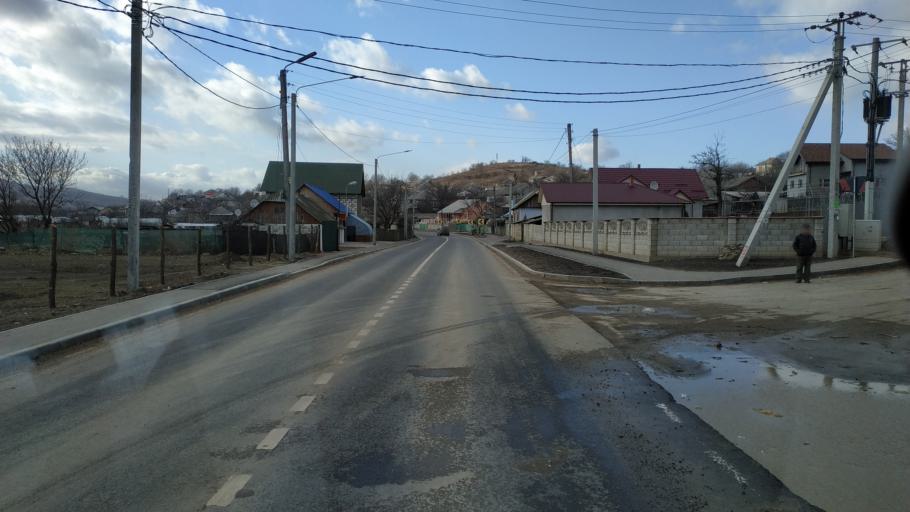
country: MD
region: Calarasi
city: Calarasi
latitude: 47.2889
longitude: 28.1945
